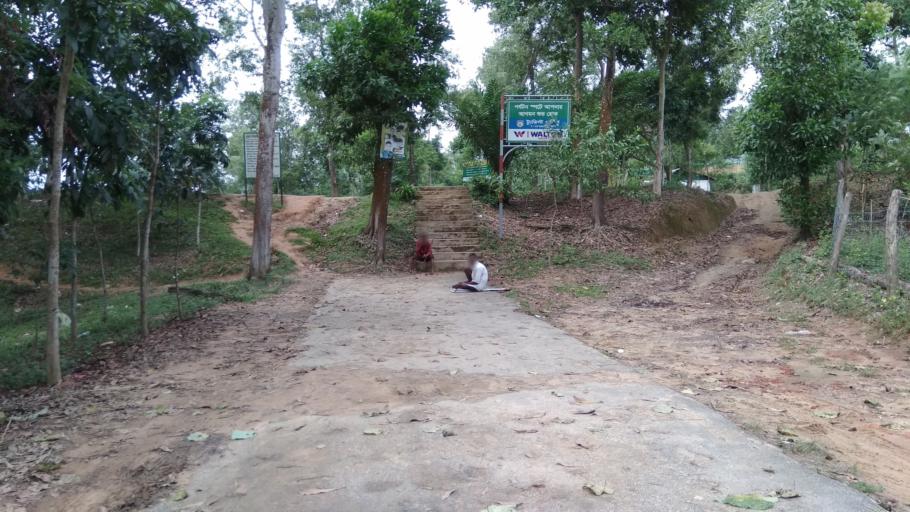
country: IN
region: Tripura
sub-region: Dhalai
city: Kamalpur
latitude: 24.2824
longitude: 91.8219
